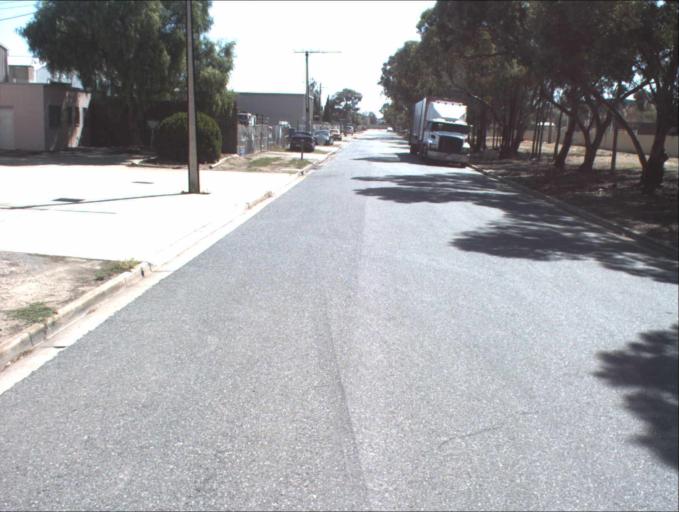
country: AU
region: South Australia
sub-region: Charles Sturt
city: Woodville North
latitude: -34.8370
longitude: 138.5560
